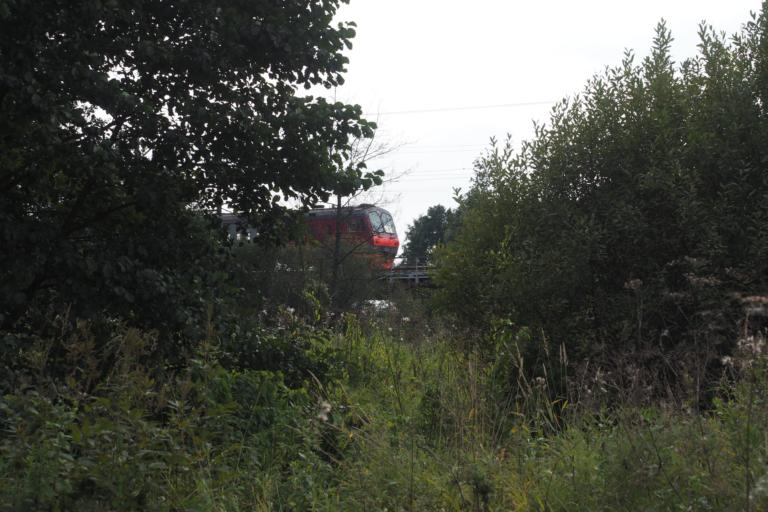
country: RU
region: Moskovskaya
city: Malyshevo
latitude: 55.5333
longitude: 38.3114
